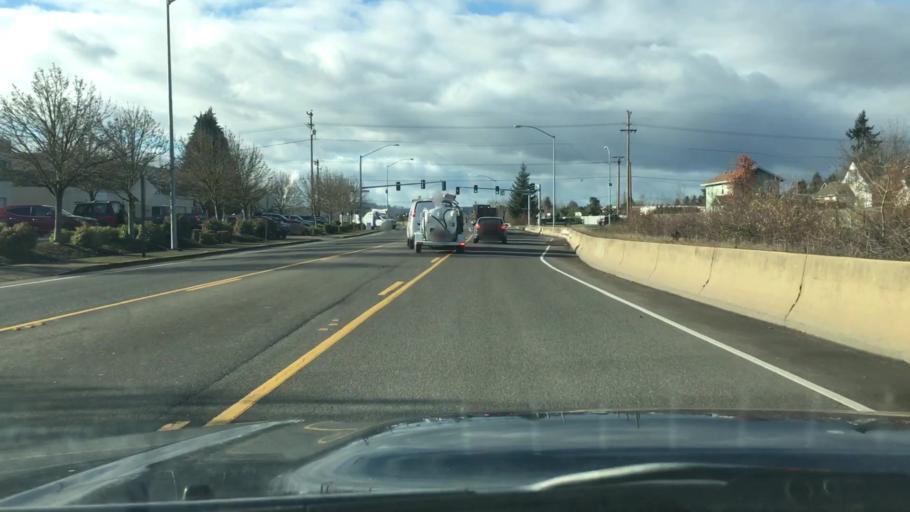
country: US
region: Oregon
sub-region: Lane County
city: Eugene
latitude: 44.0645
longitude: -123.1614
